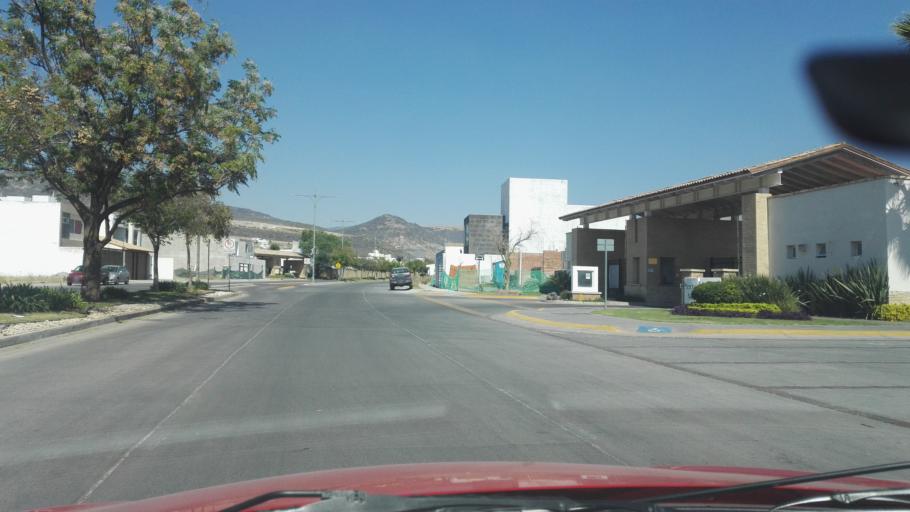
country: MX
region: Guanajuato
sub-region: Leon
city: Medina
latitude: 21.1267
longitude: -101.6109
